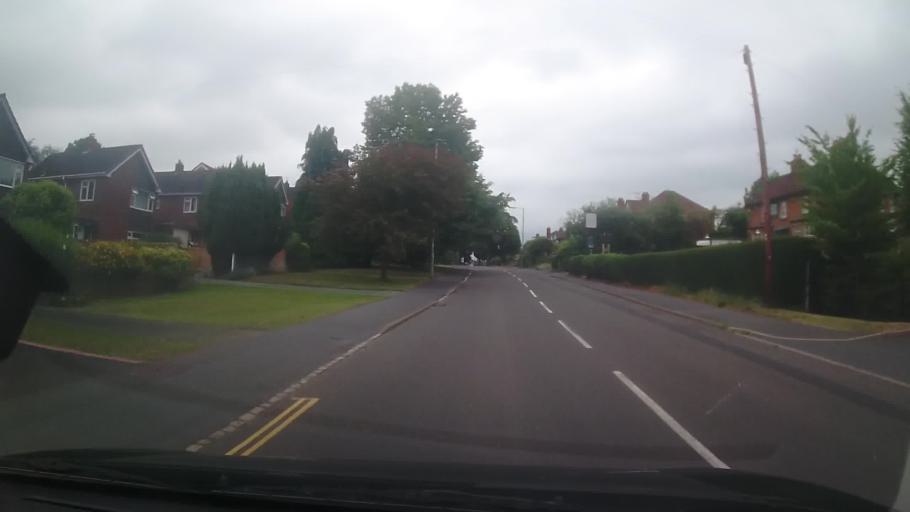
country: GB
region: England
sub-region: Shropshire
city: Shrewsbury
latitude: 52.7103
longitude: -2.7768
